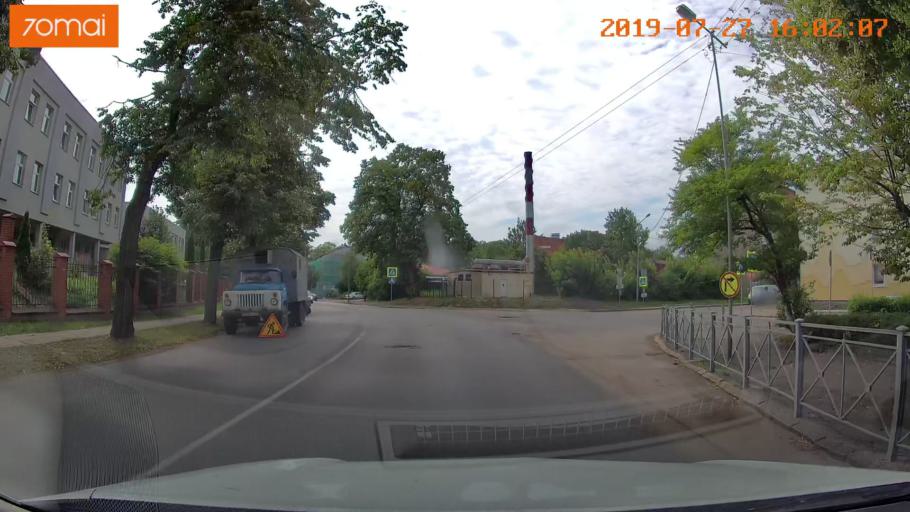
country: RU
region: Kaliningrad
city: Chernyakhovsk
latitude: 54.6307
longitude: 21.8136
